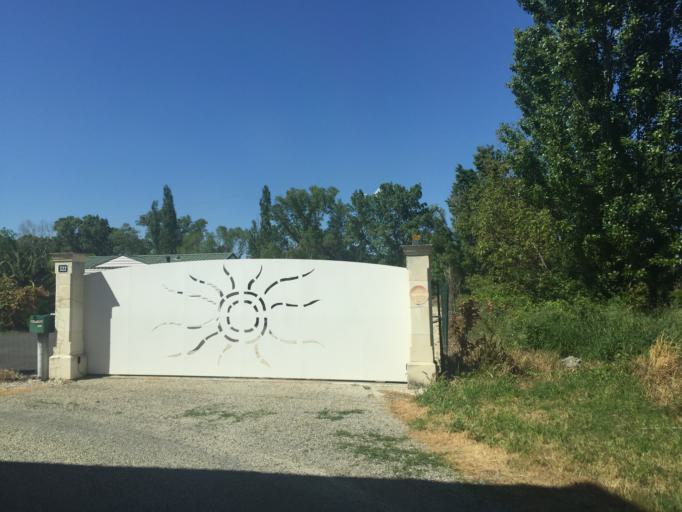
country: FR
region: Provence-Alpes-Cote d'Azur
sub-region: Departement du Vaucluse
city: Orange
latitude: 44.1472
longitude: 4.7790
